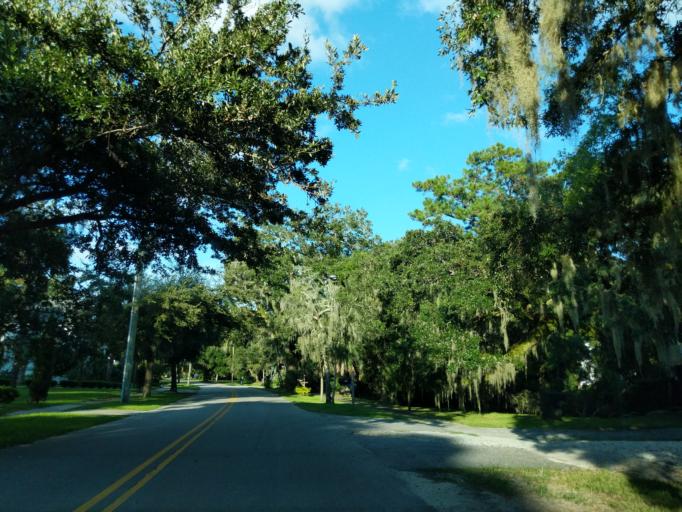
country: US
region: South Carolina
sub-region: Charleston County
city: Awendaw
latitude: 33.0845
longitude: -79.4634
